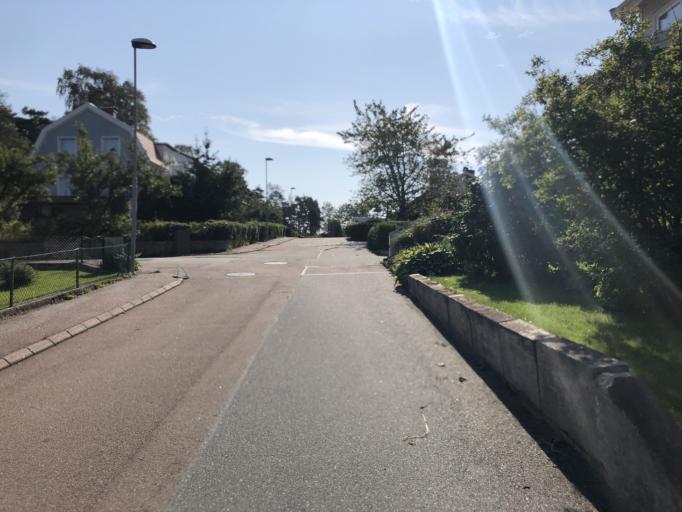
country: SE
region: Vaestra Goetaland
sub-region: Goteborg
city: Goeteborg
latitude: 57.7389
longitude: 11.9687
